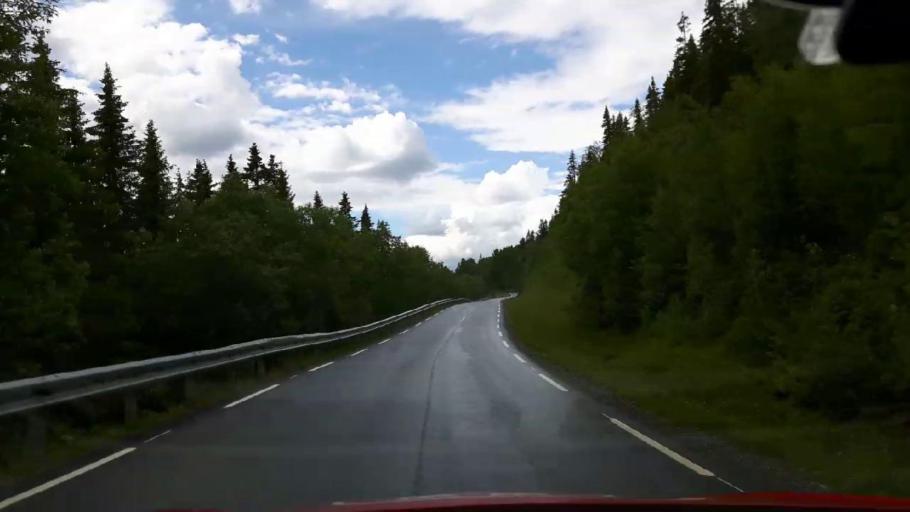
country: NO
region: Nord-Trondelag
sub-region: Lierne
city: Sandvika
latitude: 64.1040
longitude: 13.9960
